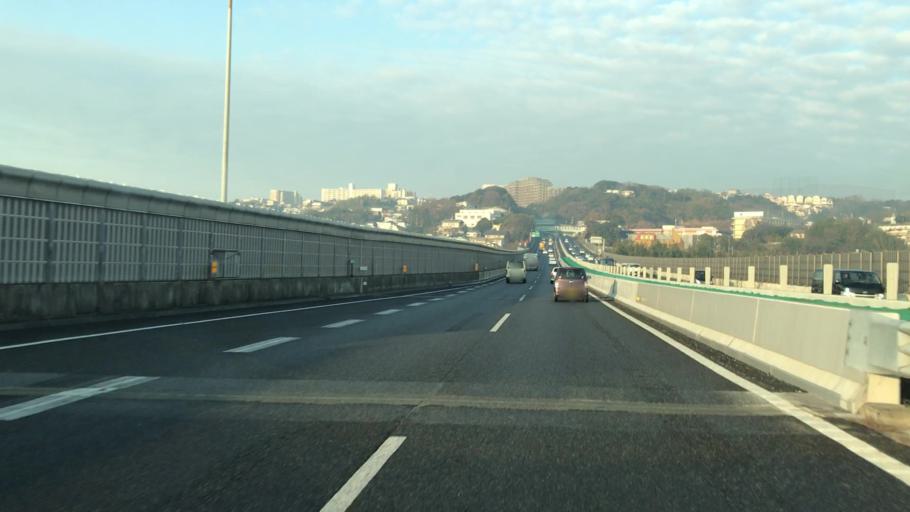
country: JP
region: Hyogo
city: Akashi
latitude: 34.6477
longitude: 135.0701
